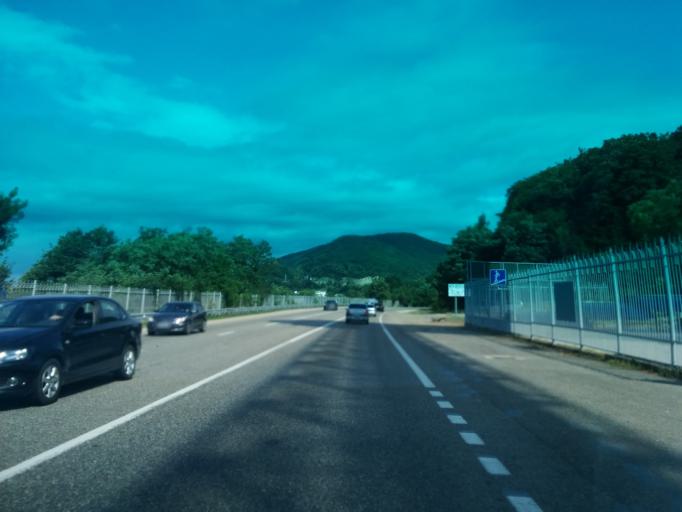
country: RU
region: Krasnodarskiy
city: Nebug
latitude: 44.1578
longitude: 39.0031
